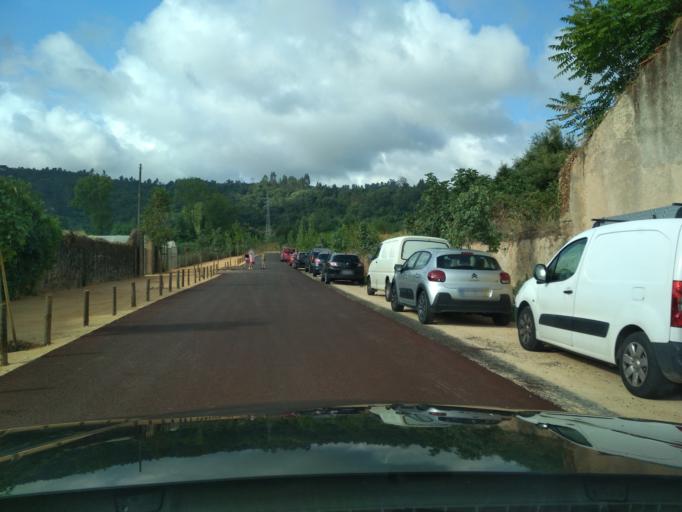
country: PT
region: Coimbra
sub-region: Coimbra
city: Coimbra
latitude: 40.1831
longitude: -8.4153
